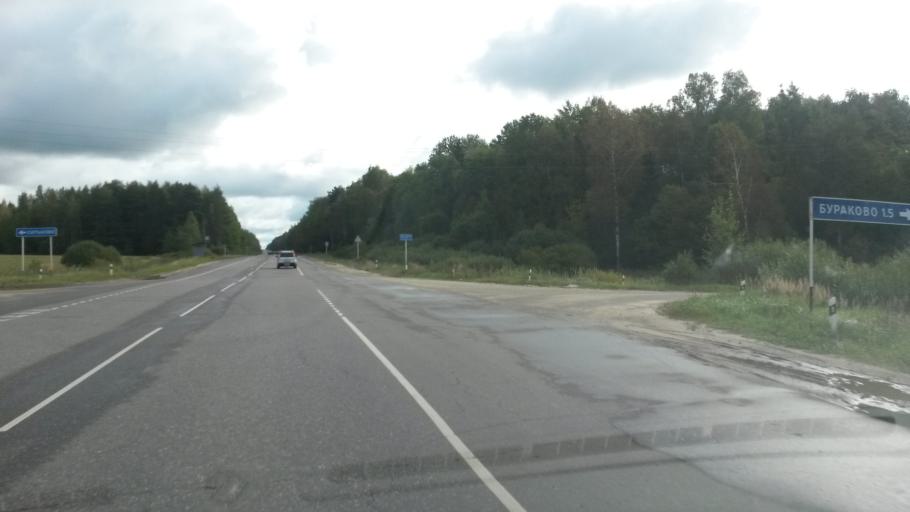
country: RU
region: Ivanovo
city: Kaminskiy
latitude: 57.0733
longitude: 41.4390
